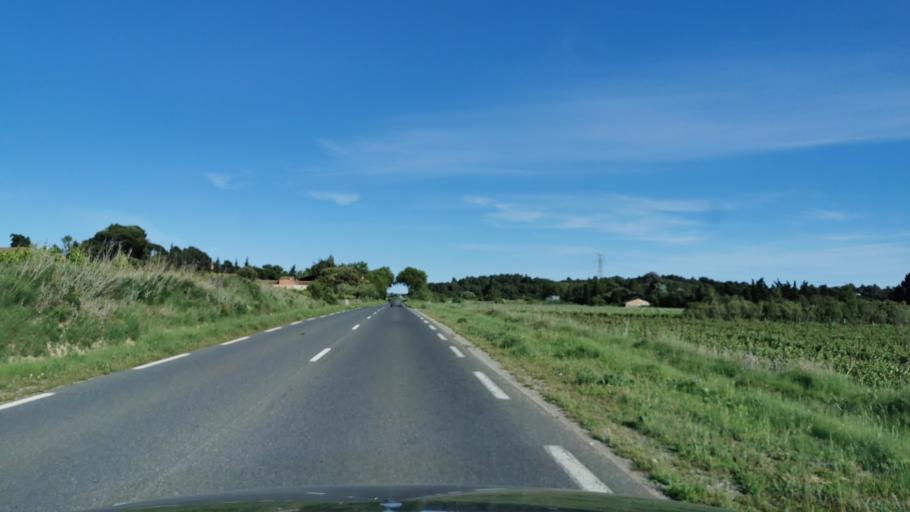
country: FR
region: Languedoc-Roussillon
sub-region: Departement de l'Aude
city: Moussan
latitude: 43.2085
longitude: 2.9510
